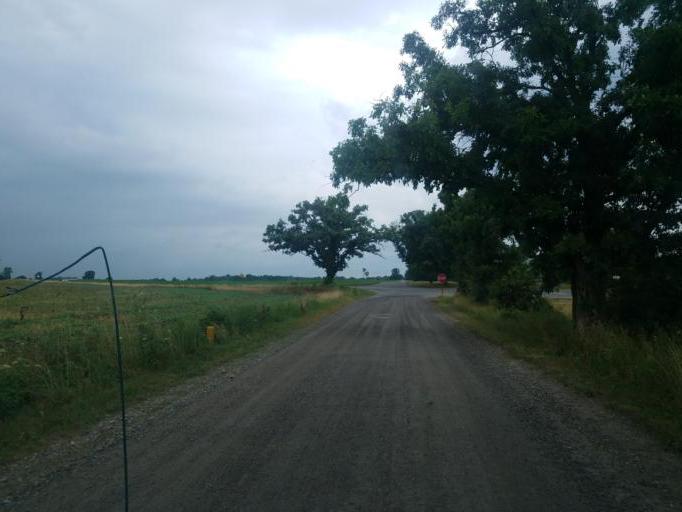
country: US
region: Ohio
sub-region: Defiance County
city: Hicksville
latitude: 41.3242
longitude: -84.8040
